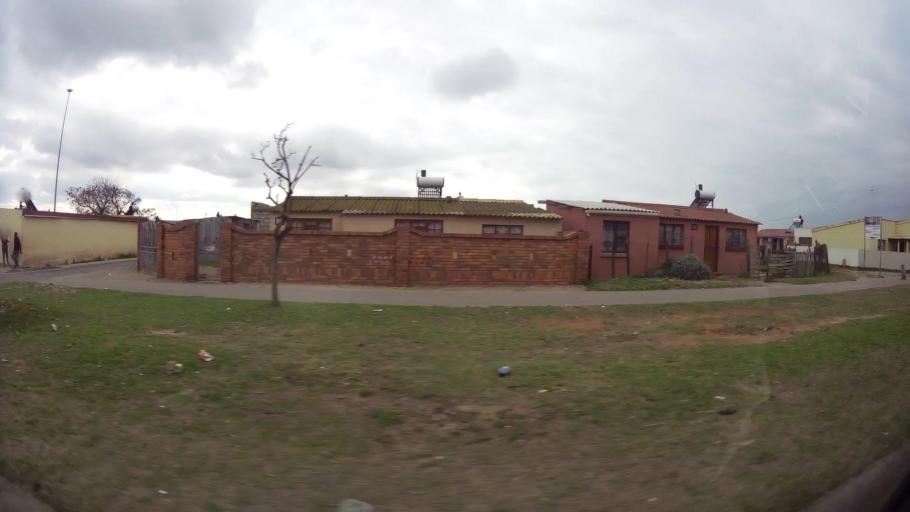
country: ZA
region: Eastern Cape
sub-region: Nelson Mandela Bay Metropolitan Municipality
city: Port Elizabeth
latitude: -33.8764
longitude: 25.5886
